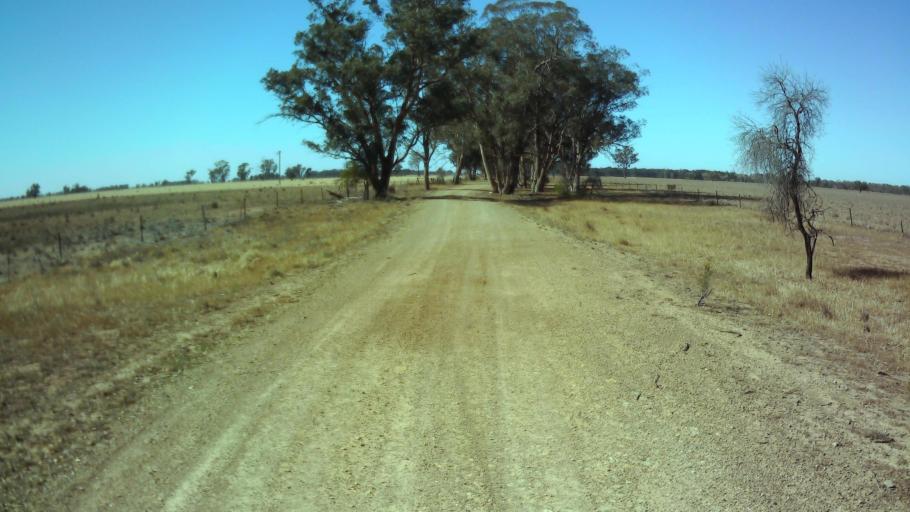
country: AU
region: New South Wales
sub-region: Weddin
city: Grenfell
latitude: -33.9454
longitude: 147.8701
